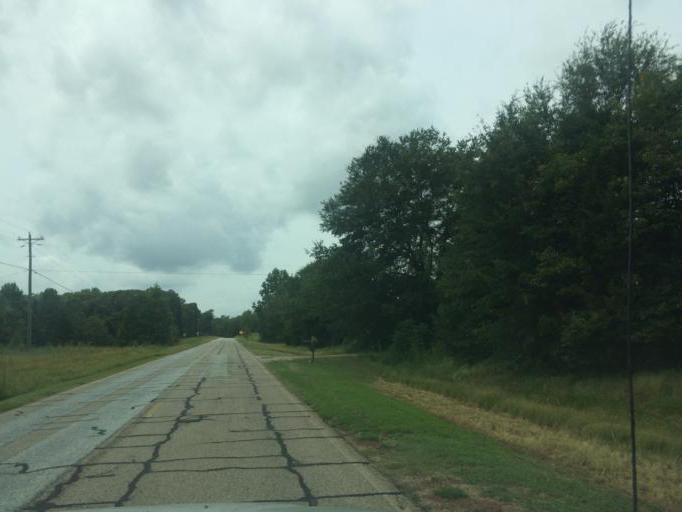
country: US
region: Georgia
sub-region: Hart County
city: Hartwell
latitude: 34.2872
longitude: -82.8511
